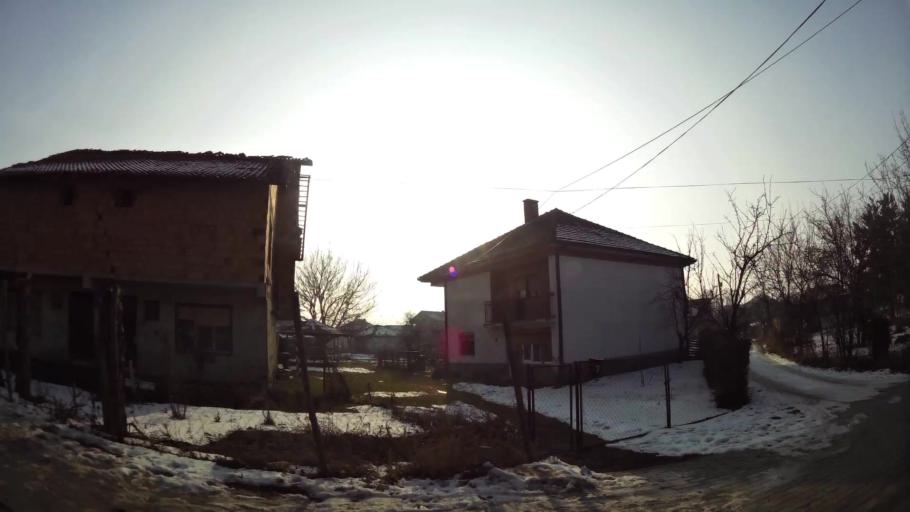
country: MK
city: Kadino
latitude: 41.9668
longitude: 21.5977
